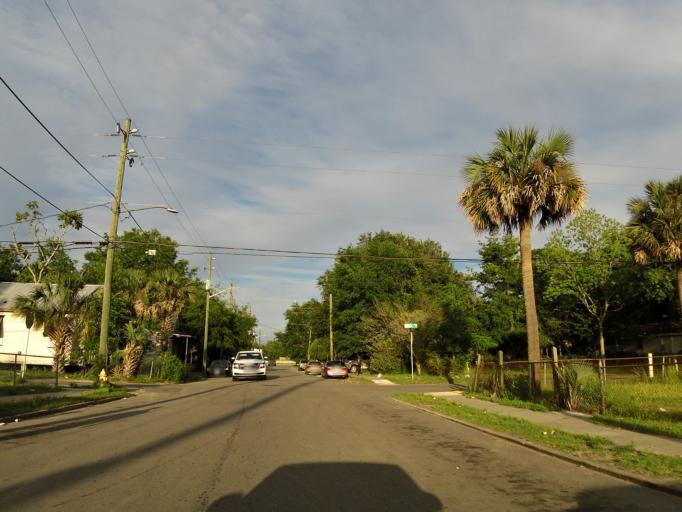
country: US
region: Florida
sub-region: Duval County
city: Jacksonville
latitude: 30.3384
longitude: -81.6390
